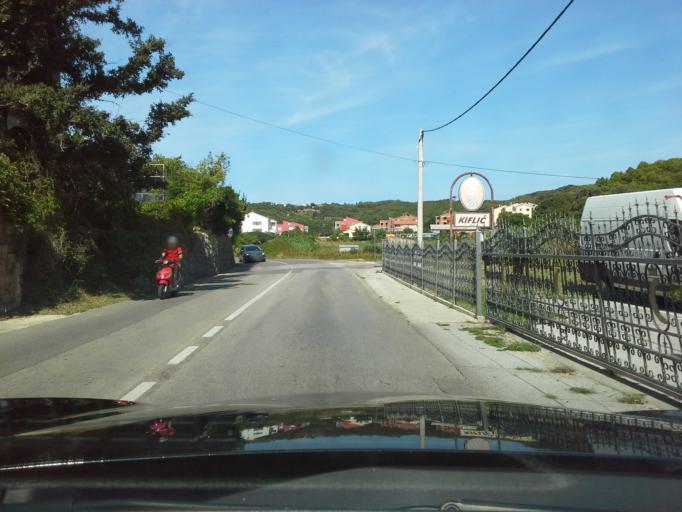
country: HR
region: Primorsko-Goranska
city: Kampor
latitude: 44.7700
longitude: 14.7489
